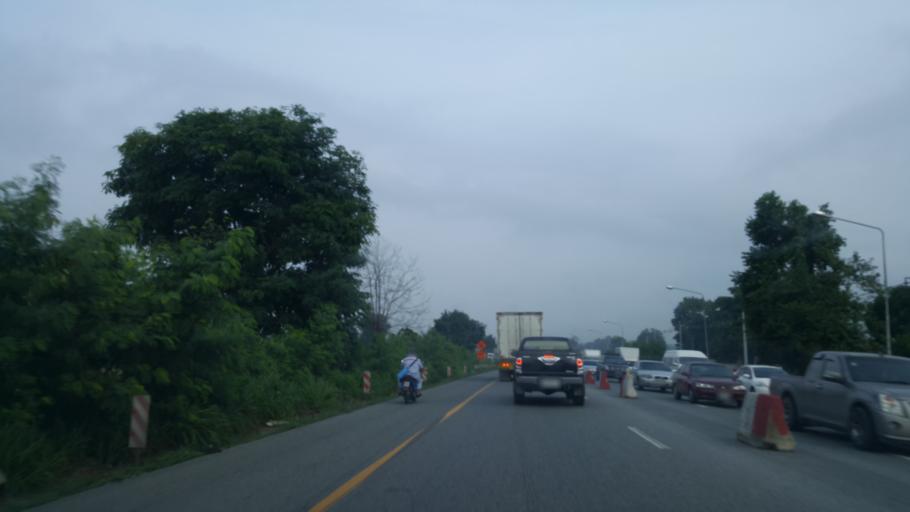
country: TH
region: Chon Buri
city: Phatthaya
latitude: 12.9313
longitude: 101.0010
